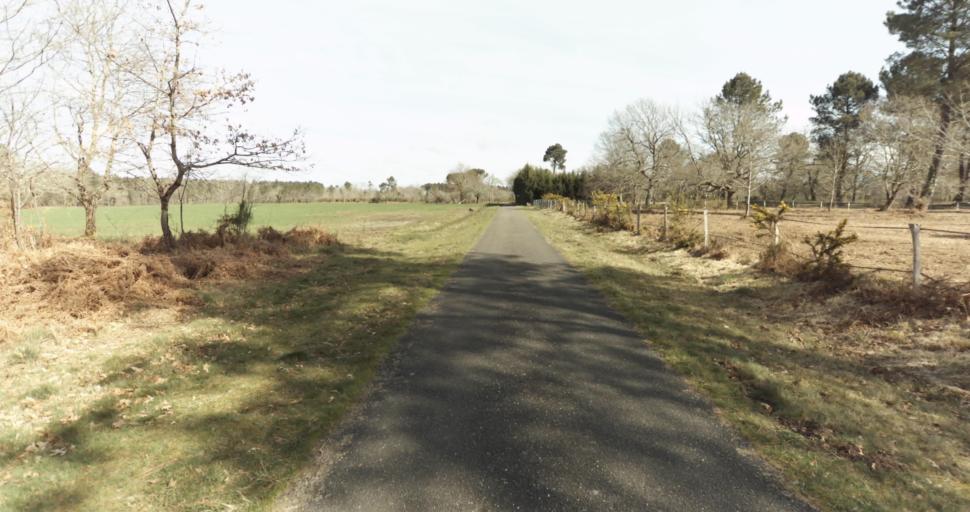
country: FR
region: Aquitaine
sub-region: Departement des Landes
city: Roquefort
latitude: 44.0750
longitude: -0.3562
